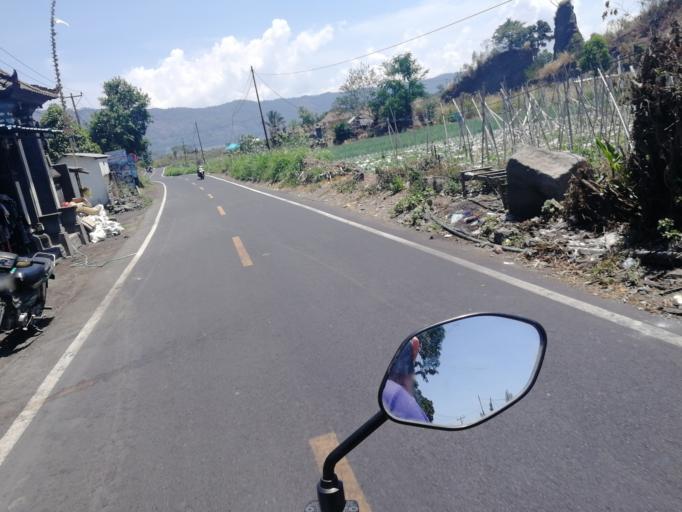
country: ID
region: Bali
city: Banjar Trunyan
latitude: -8.2386
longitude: 115.4065
